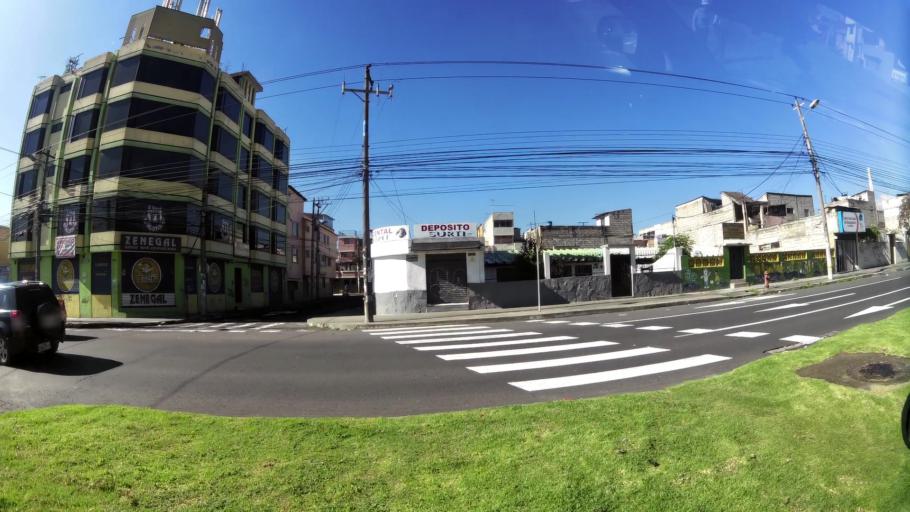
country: EC
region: Pichincha
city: Quito
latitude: -0.2502
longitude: -78.5325
